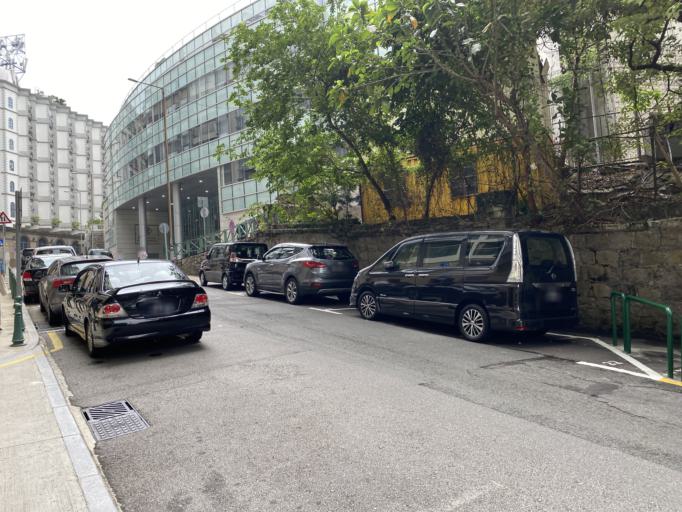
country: MO
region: Macau
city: Macau
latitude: 22.1959
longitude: 113.5475
